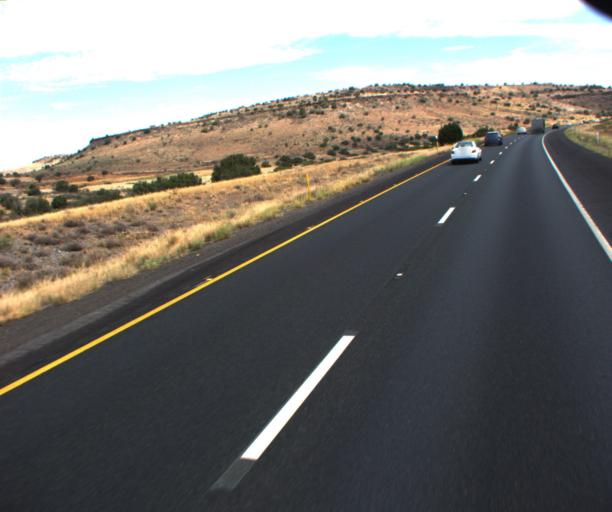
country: US
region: Arizona
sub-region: Yavapai County
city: Camp Verde
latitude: 34.4766
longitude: -112.0208
